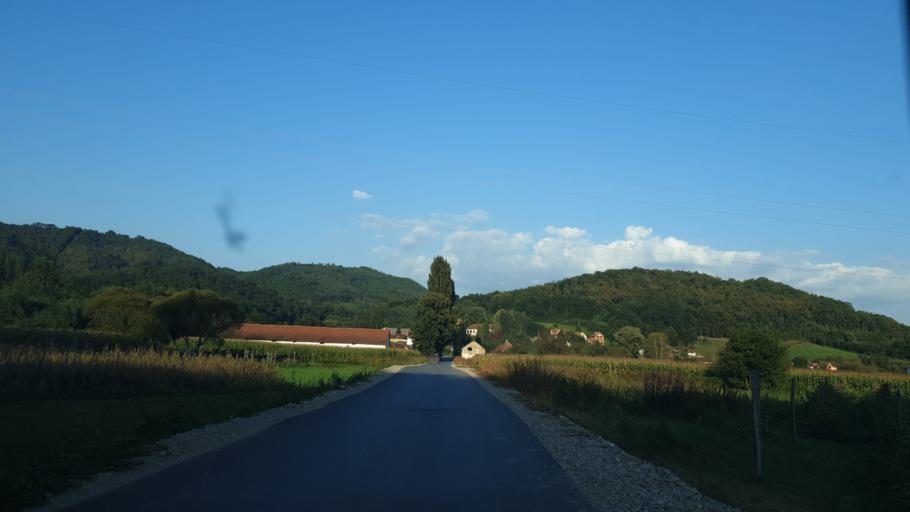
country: RS
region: Central Serbia
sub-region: Zlatiborski Okrug
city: Pozega
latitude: 43.8769
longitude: 19.9957
